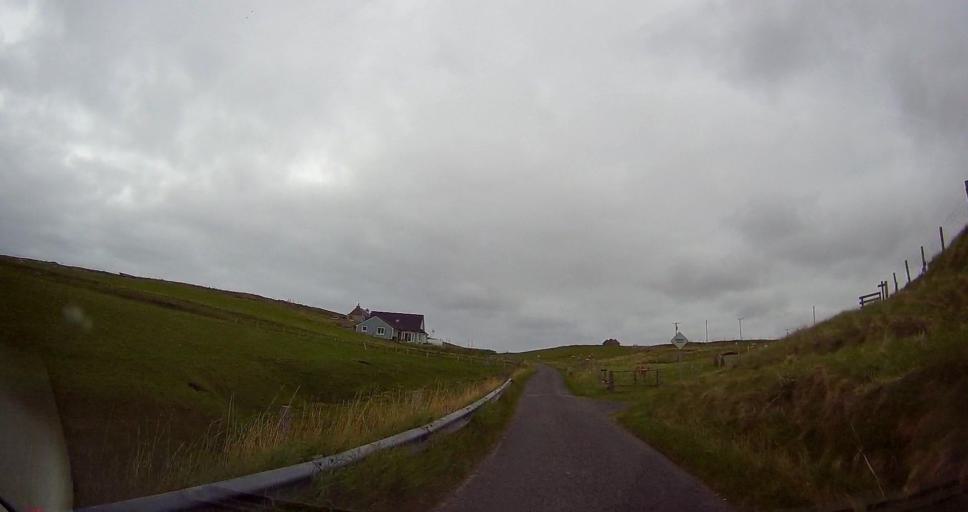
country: GB
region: Scotland
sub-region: Shetland Islands
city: Shetland
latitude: 60.8021
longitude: -0.8772
